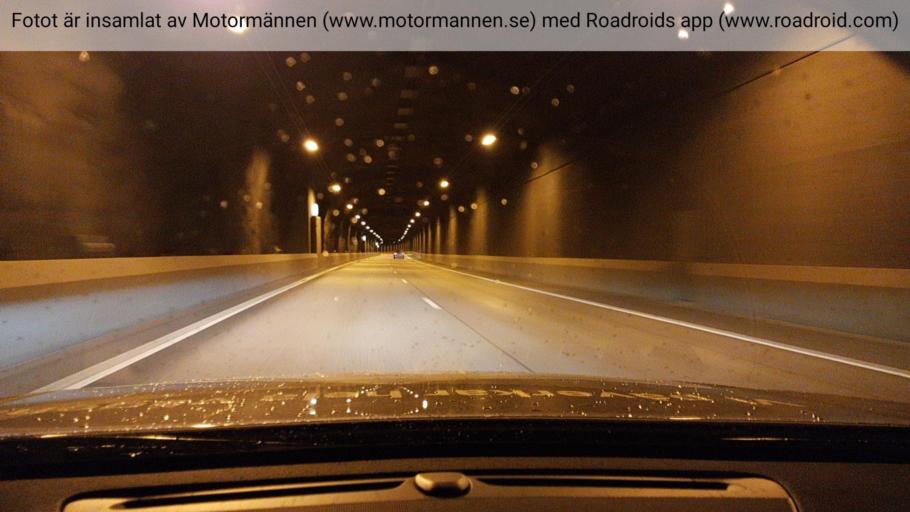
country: SE
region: Stockholm
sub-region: Sollentuna Kommun
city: Sollentuna
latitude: 59.4608
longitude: 17.9651
